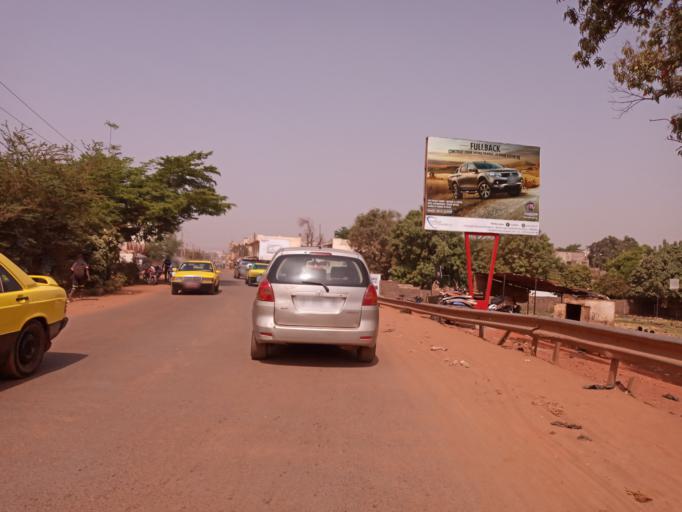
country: ML
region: Bamako
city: Bamako
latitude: 12.5888
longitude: -7.9787
